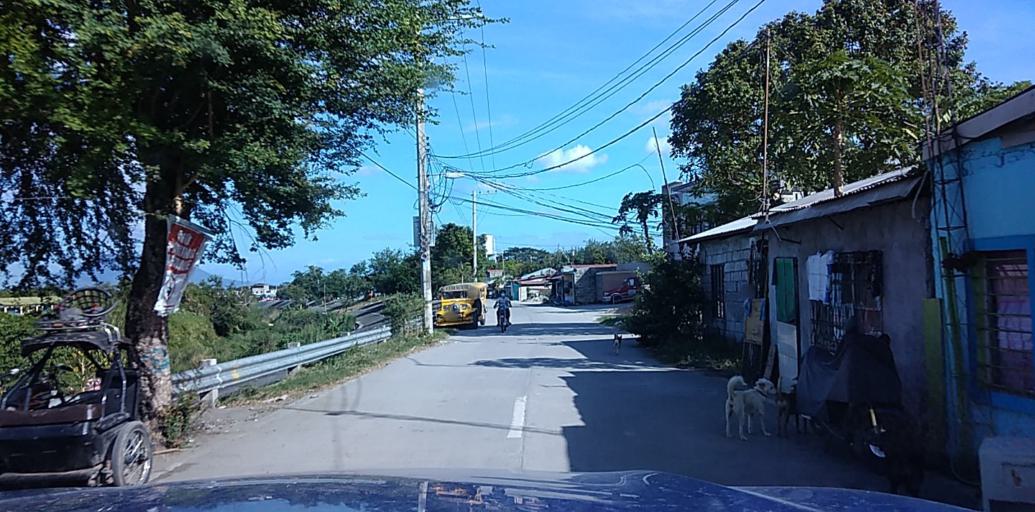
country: PH
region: Central Luzon
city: Santol
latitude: 15.1502
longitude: 120.5432
